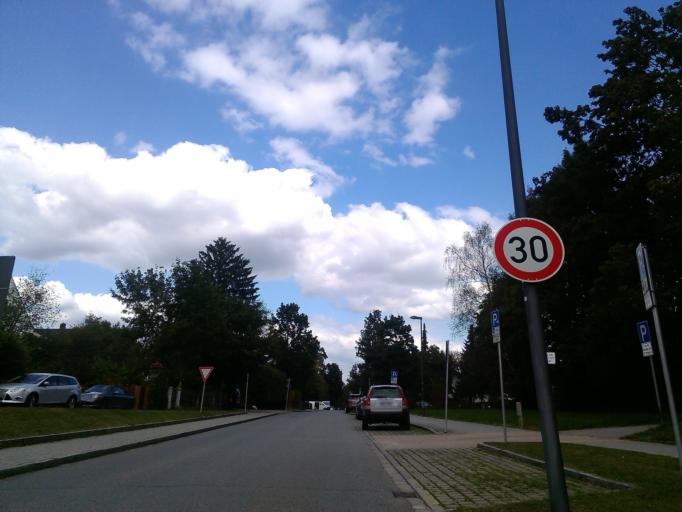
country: DE
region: Bavaria
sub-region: Upper Bavaria
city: Grafelfing
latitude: 48.1292
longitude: 11.4328
